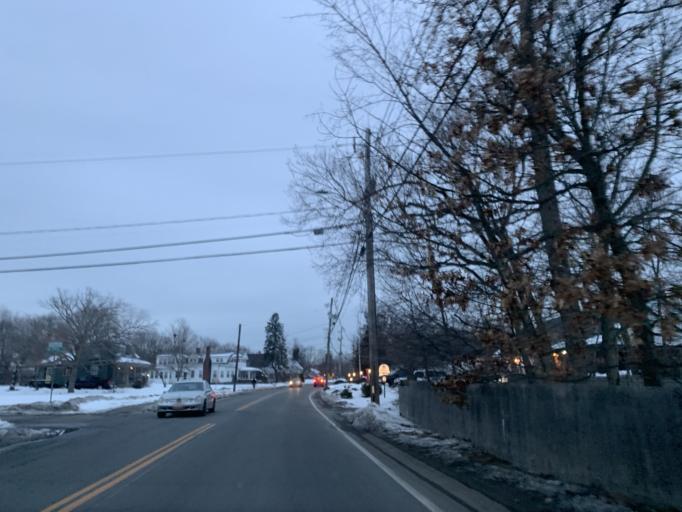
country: US
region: Massachusetts
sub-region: Norfolk County
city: Stoughton
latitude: 42.1378
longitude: -71.1136
